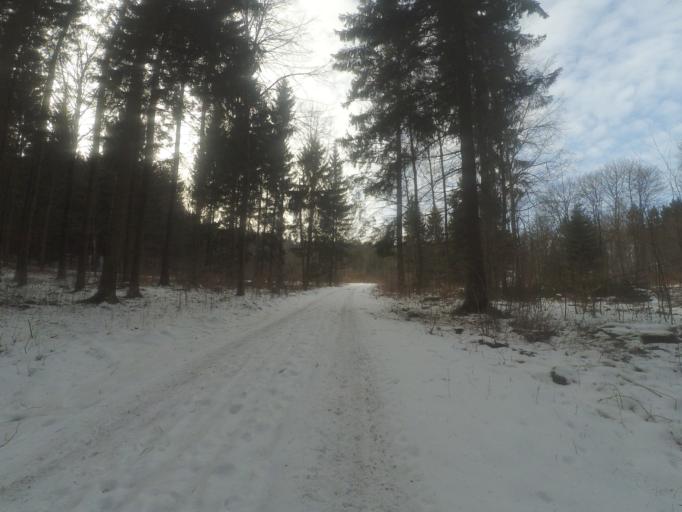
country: DE
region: Baden-Wuerttemberg
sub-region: Regierungsbezirk Stuttgart
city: Aalen
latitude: 48.8122
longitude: 10.0846
